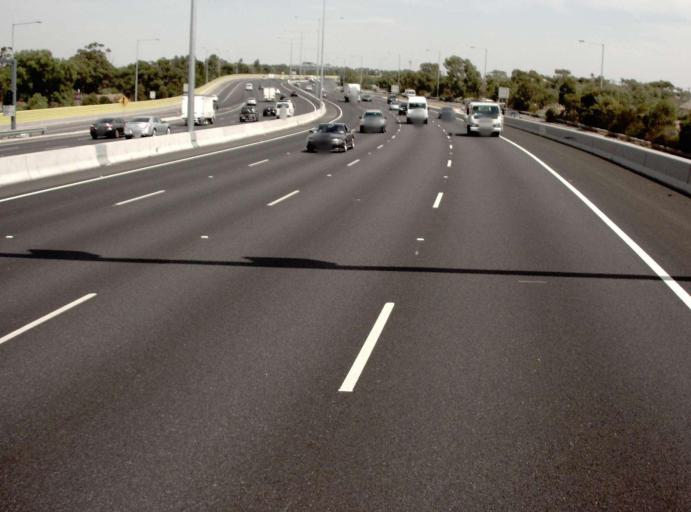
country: AU
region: Victoria
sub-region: Brimbank
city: Deer Park
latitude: -37.7725
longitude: 144.7940
